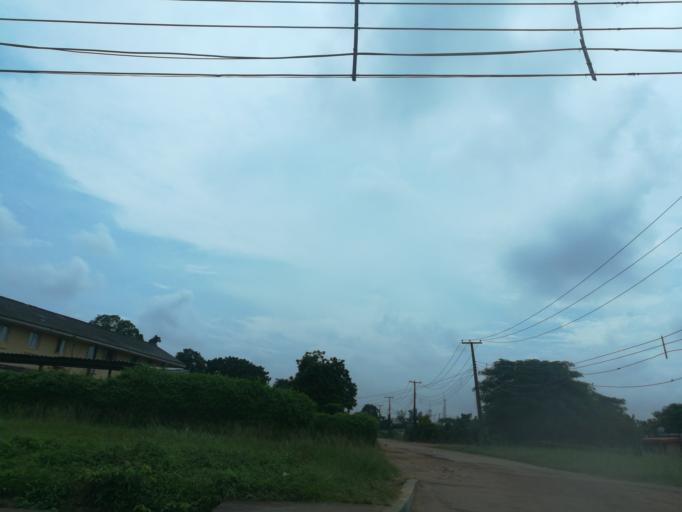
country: NG
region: Lagos
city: Oshodi
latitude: 6.5668
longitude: 3.3610
